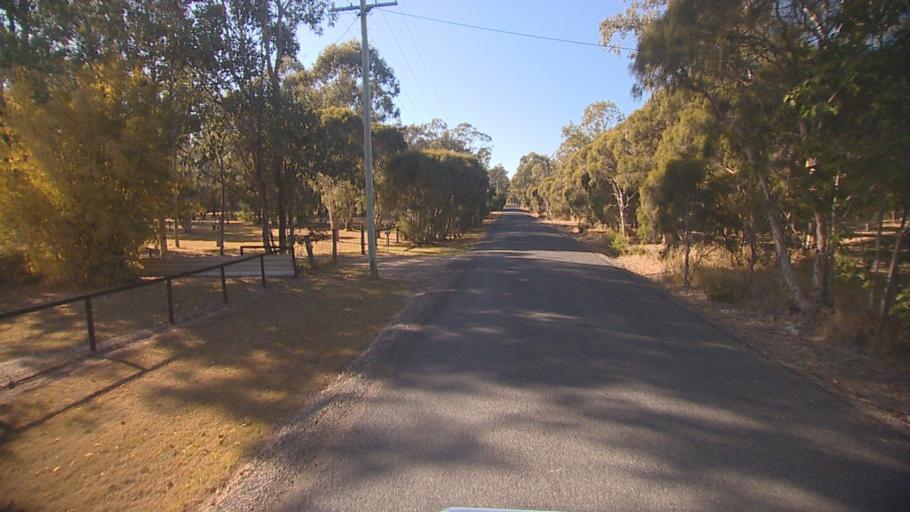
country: AU
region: Queensland
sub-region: Logan
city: Cedar Vale
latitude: -27.8379
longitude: 152.9982
